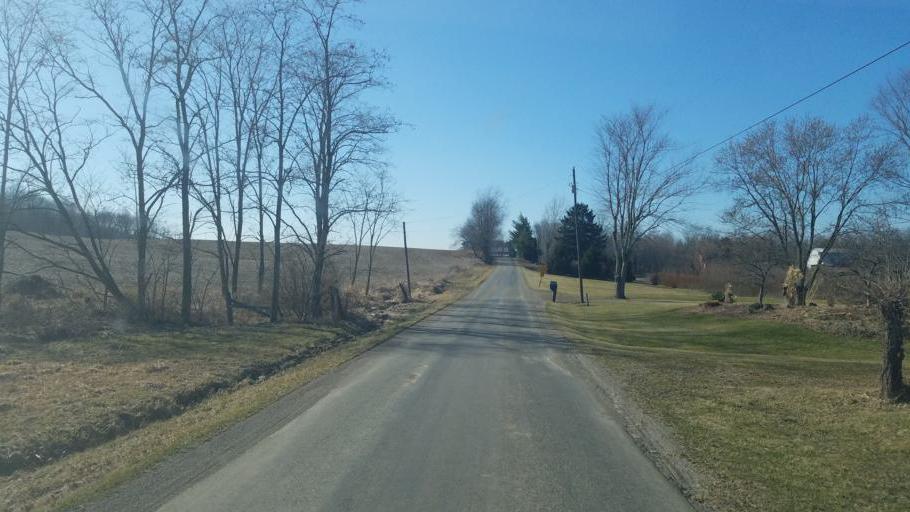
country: US
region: Ohio
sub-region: Sandusky County
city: Bellville
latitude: 40.5751
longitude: -82.5894
